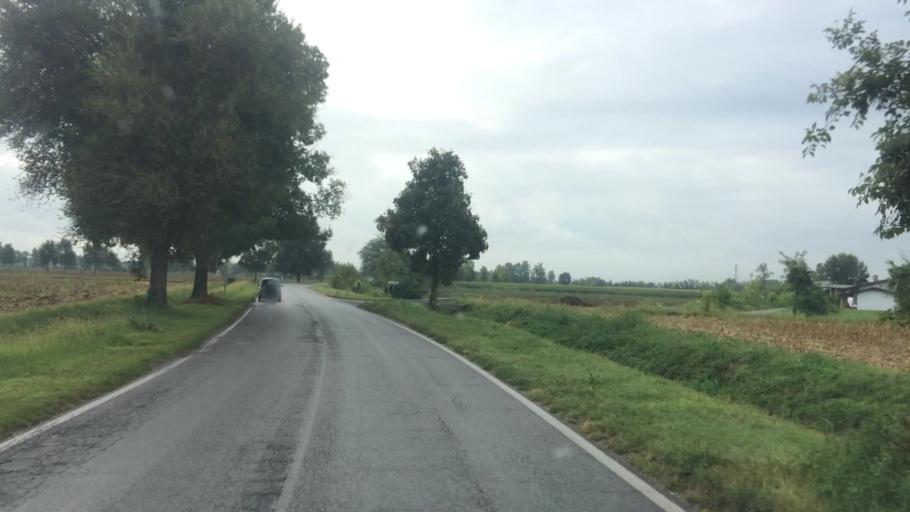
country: IT
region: Lombardy
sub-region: Provincia di Brescia
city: Longhena
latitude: 45.4305
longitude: 10.0630
